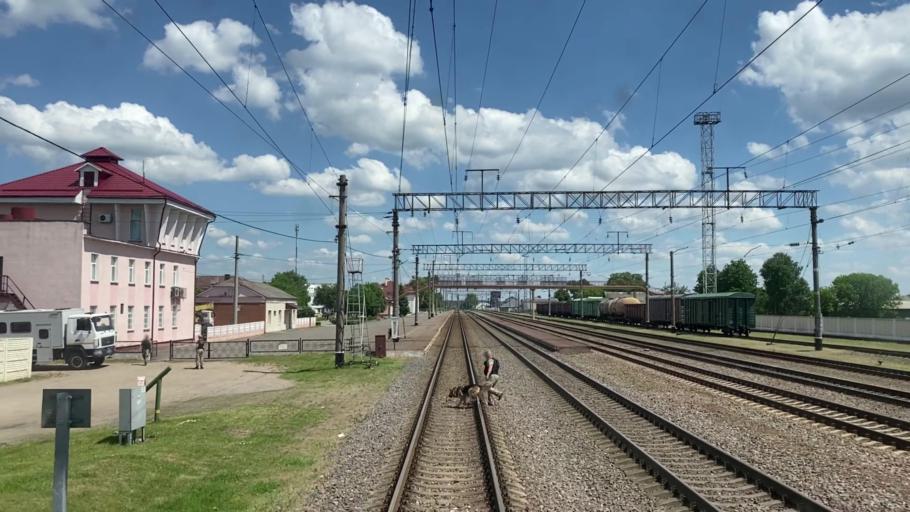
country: BY
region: Brest
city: Ivatsevichy
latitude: 52.7079
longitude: 25.3420
